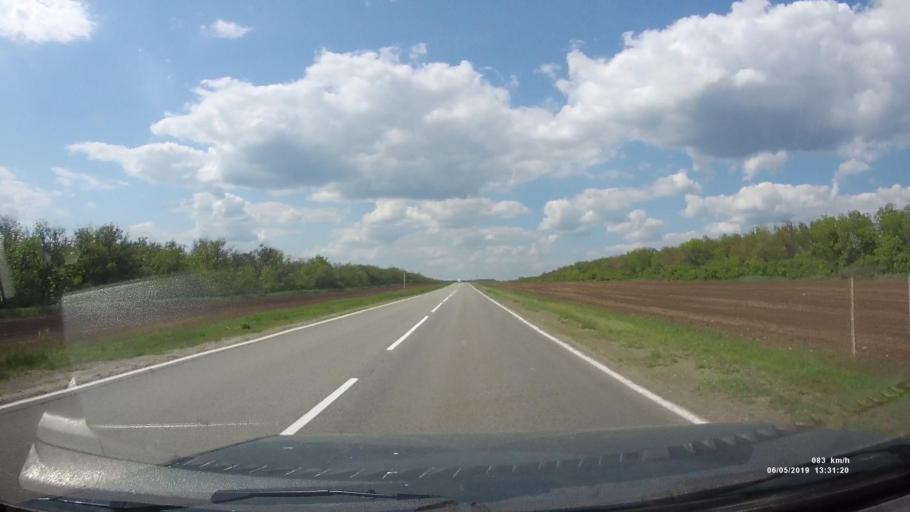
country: RU
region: Rostov
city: Ust'-Donetskiy
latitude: 47.6761
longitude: 40.8119
